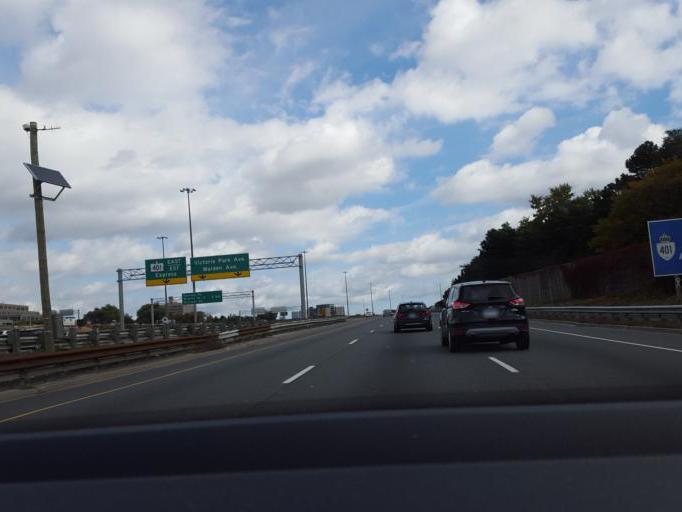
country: CA
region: Ontario
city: Willowdale
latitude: 43.7674
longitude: -79.3341
